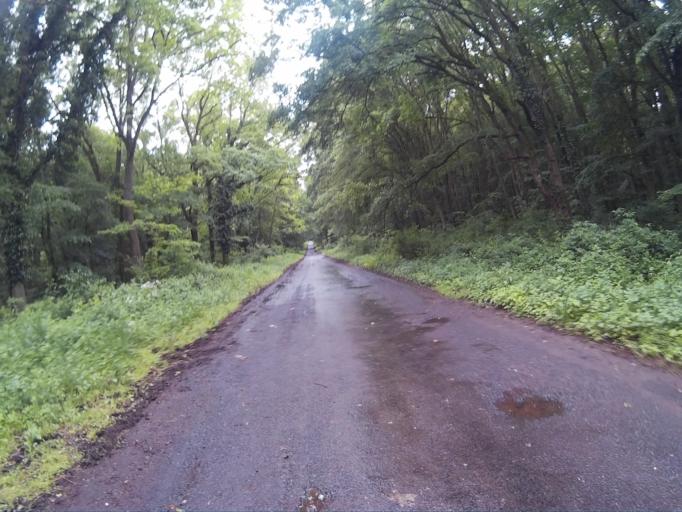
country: HU
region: Veszprem
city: Sumeg
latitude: 46.9395
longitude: 17.2906
